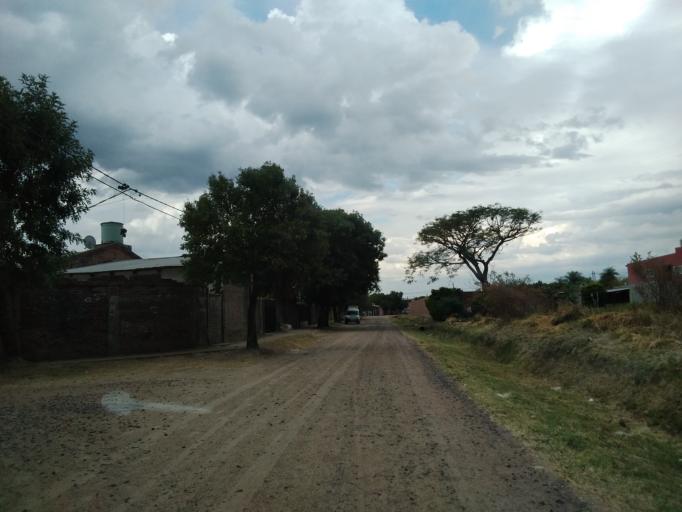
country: AR
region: Corrientes
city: Corrientes
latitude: -27.5226
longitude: -58.7947
